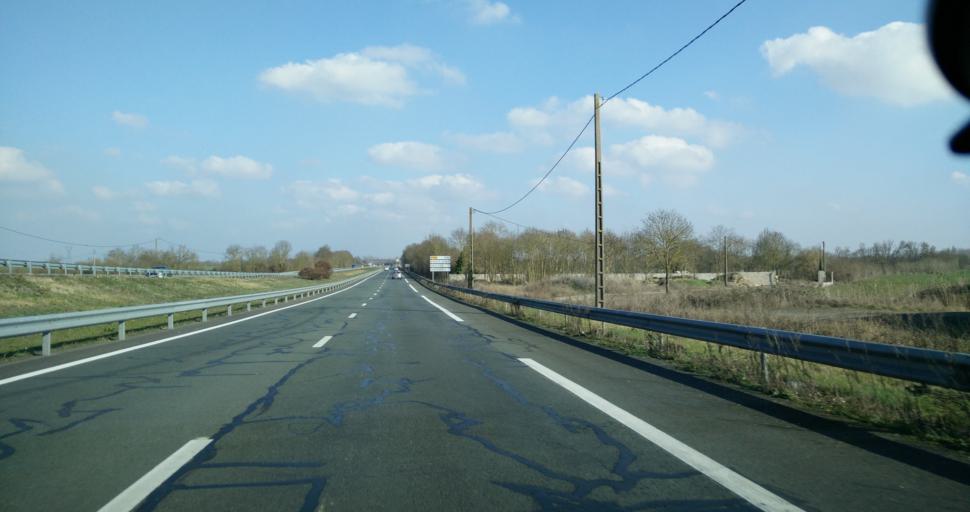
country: FR
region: Poitou-Charentes
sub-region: Departement de la Charente-Maritime
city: Verines
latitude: 46.2221
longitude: -0.9629
